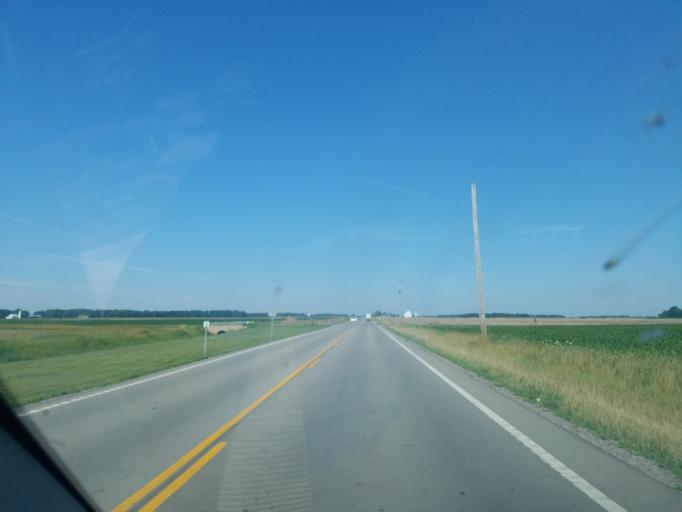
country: US
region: Ohio
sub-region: Logan County
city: Lakeview
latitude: 40.4393
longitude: -83.9639
